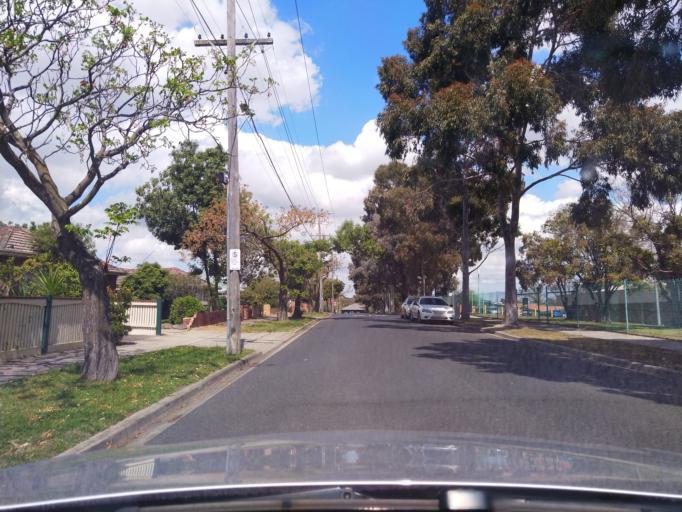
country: AU
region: Victoria
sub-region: Banyule
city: Bellfield
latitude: -37.7560
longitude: 145.0497
